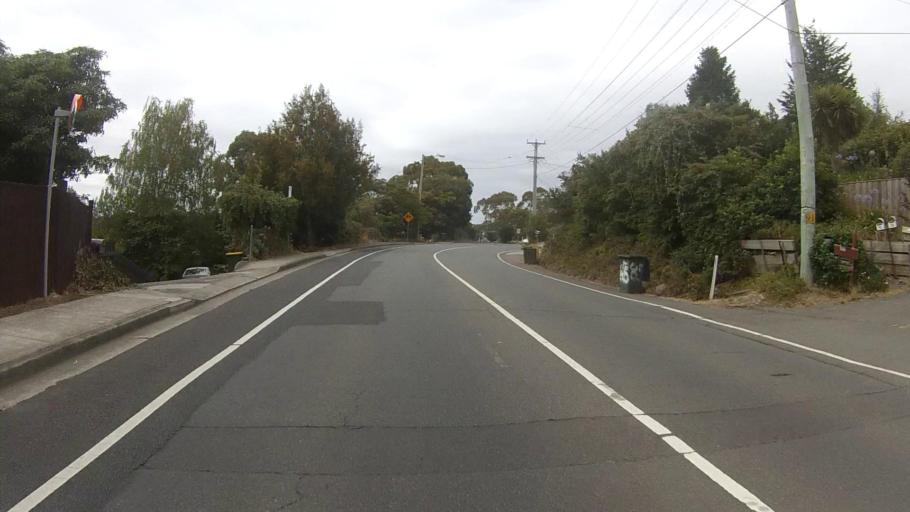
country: AU
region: Tasmania
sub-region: Kingborough
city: Taroona
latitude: -42.9374
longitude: 147.3531
